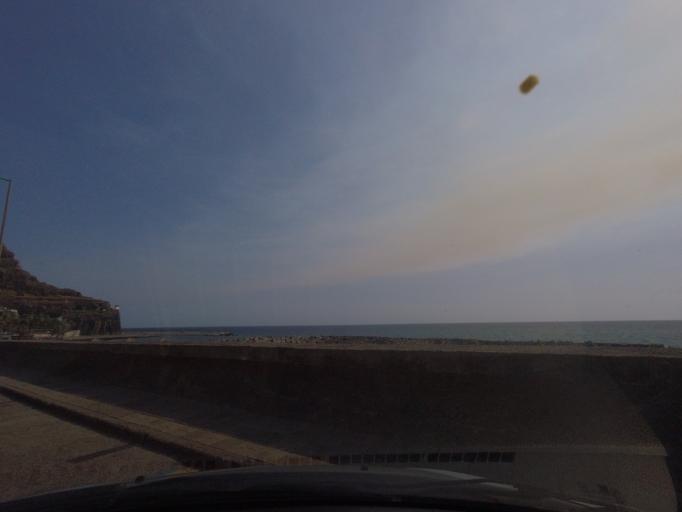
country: PT
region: Madeira
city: Ribeira Brava
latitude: 32.6720
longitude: -17.0679
